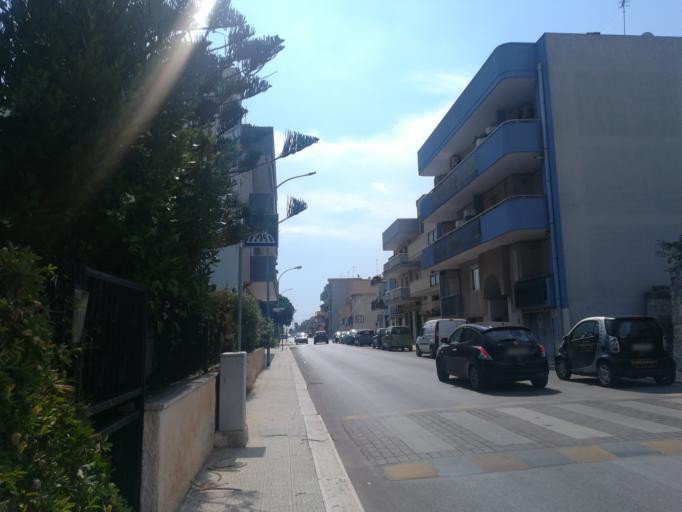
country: IT
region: Apulia
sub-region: Provincia di Bari
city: Polignano a Mare
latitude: 40.9915
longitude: 17.2262
